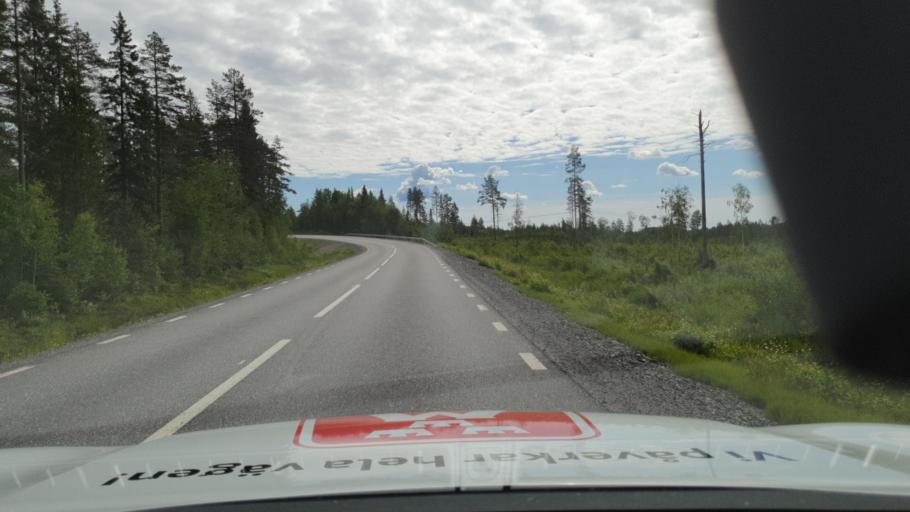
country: SE
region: Vaesterbotten
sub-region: Umea Kommun
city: Ersmark
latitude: 64.2515
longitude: 20.1448
